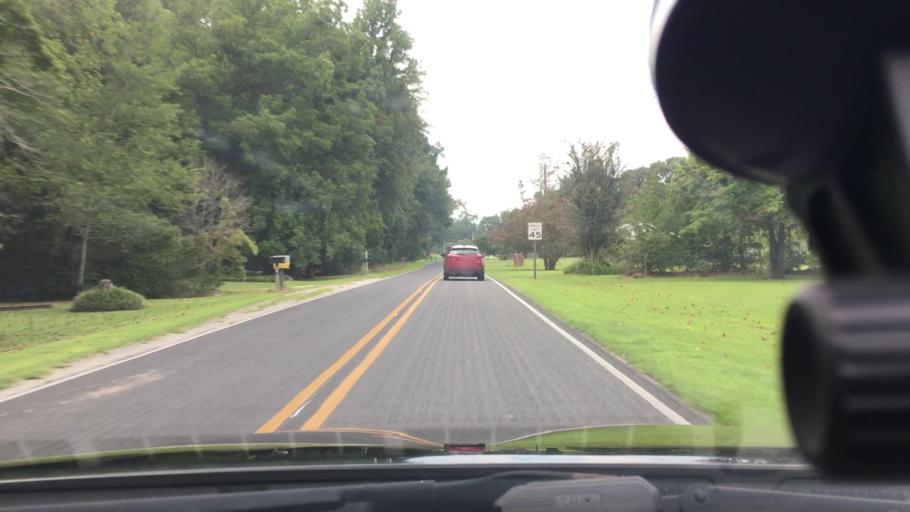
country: US
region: North Carolina
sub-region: Craven County
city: New Bern
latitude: 35.1808
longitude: -77.0565
